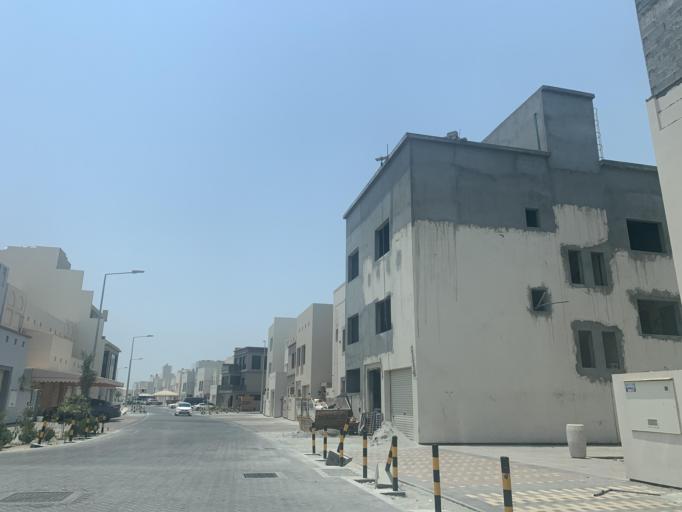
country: BH
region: Muharraq
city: Al Hadd
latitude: 26.2343
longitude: 50.6725
